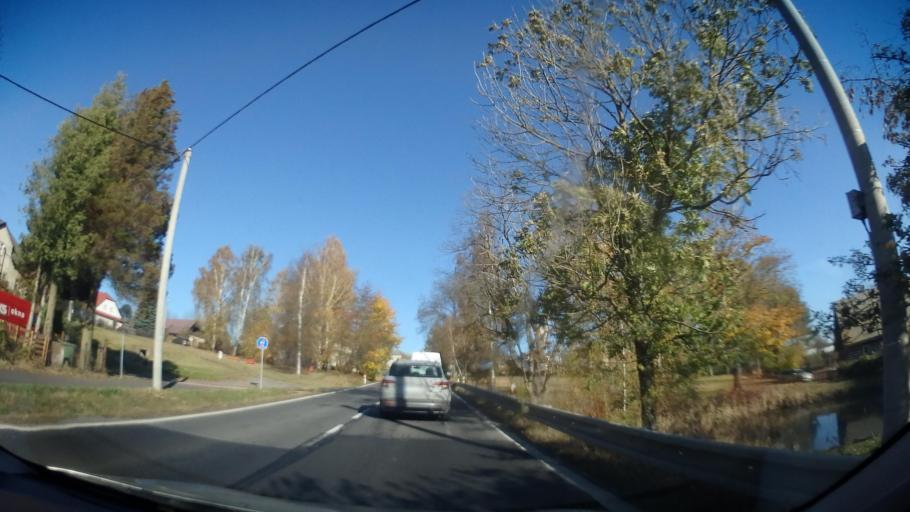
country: CZ
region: Pardubicky
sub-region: Okres Chrudim
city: Nasavrky
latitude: 49.8042
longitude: 15.8128
